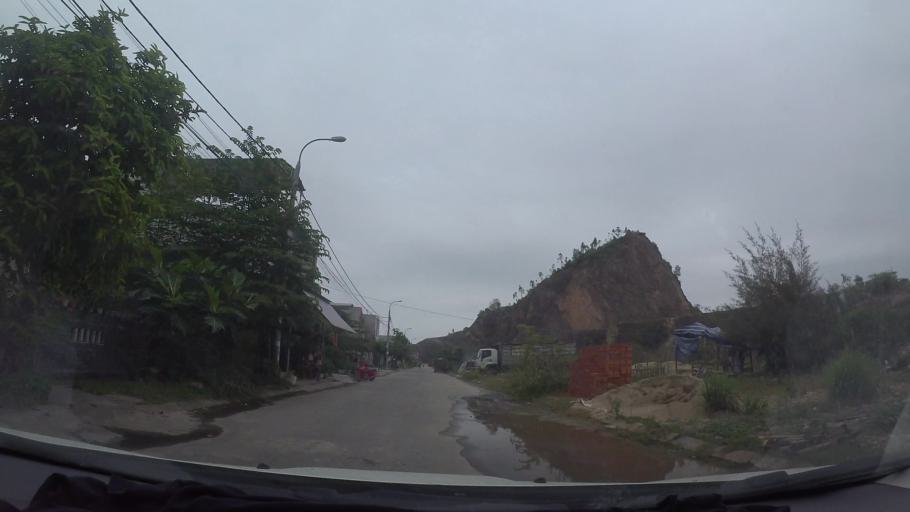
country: VN
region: Da Nang
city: Lien Chieu
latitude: 16.0659
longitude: 108.1444
